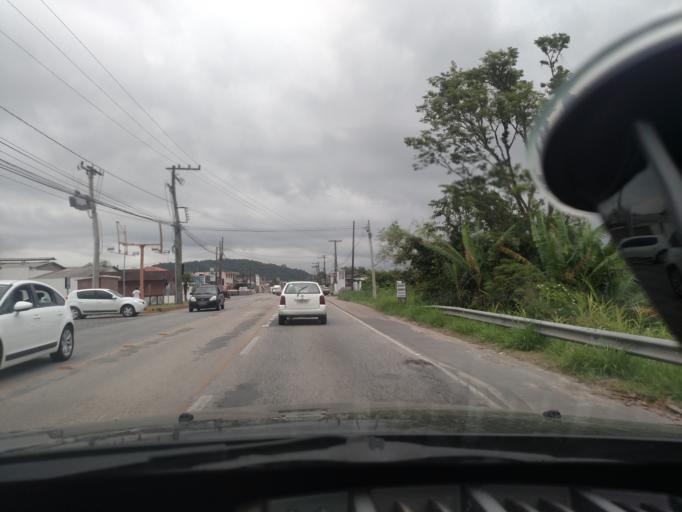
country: BR
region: Santa Catarina
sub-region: Gaspar
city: Gaspar
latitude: -26.9173
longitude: -48.9770
